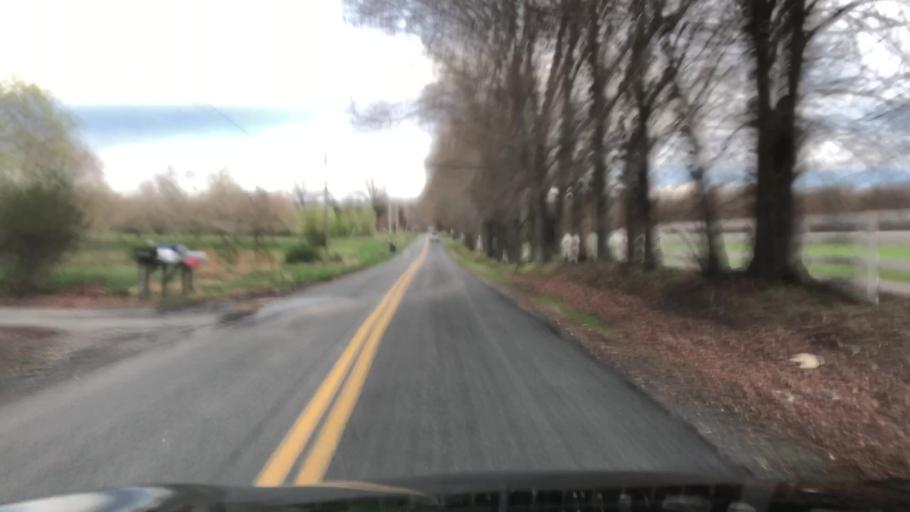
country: US
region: Virginia
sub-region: Fauquier County
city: New Baltimore
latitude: 38.7343
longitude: -77.6722
